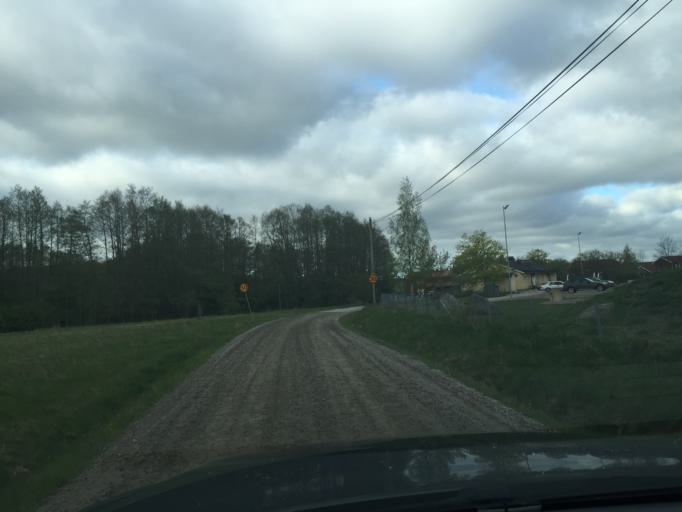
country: SE
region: Vaestmanland
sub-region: Vasteras
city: Tillberga
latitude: 59.6023
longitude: 16.7039
